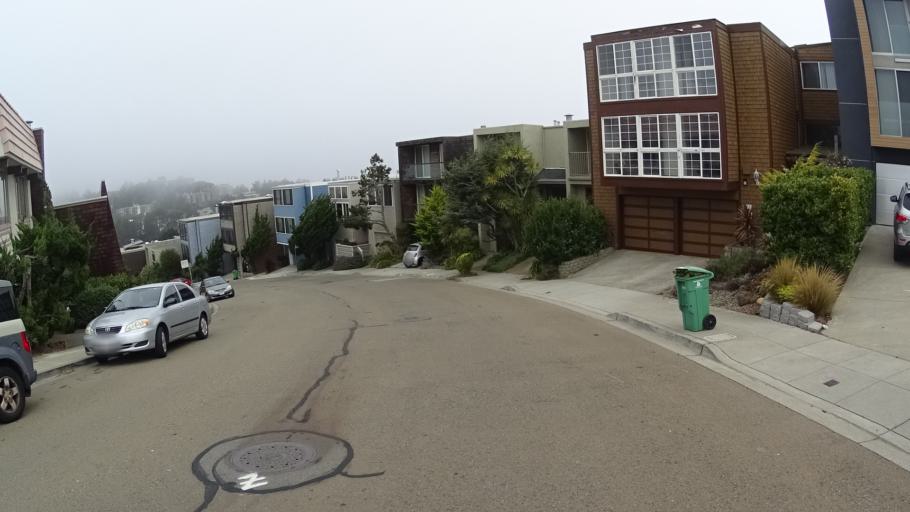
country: US
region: California
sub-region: San Francisco County
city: San Francisco
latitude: 37.7417
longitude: -122.4379
